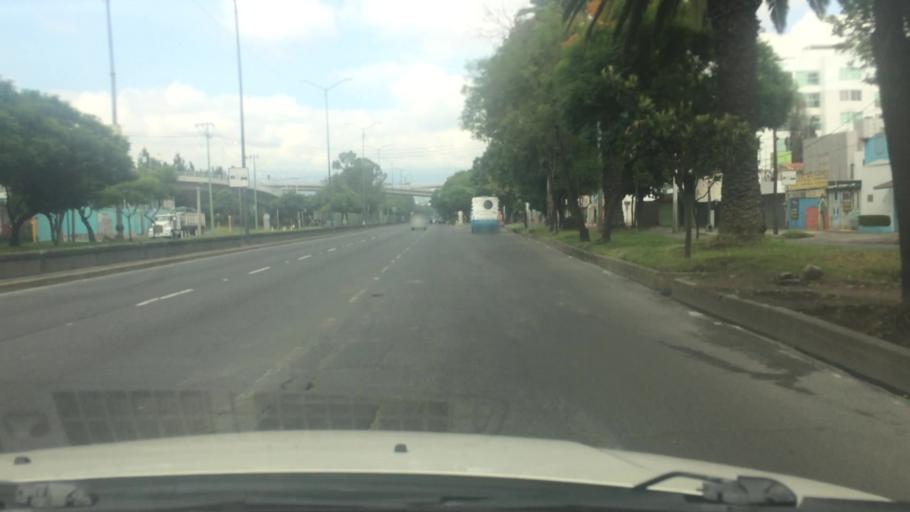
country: MX
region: Mexico City
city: Xochimilco
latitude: 19.2907
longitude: -99.1120
